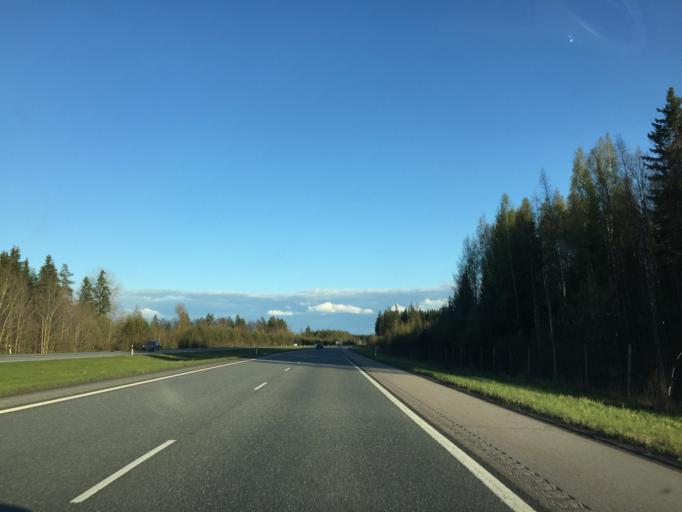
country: FI
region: Haeme
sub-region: Riihimaeki
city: Riihimaeki
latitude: 60.7825
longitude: 24.7057
